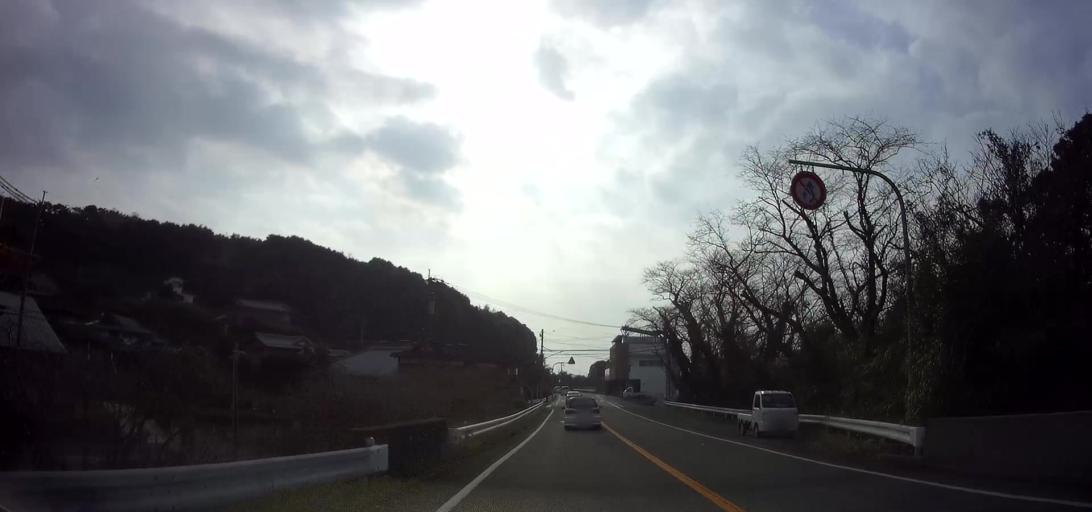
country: JP
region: Nagasaki
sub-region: Isahaya-shi
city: Isahaya
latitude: 32.7987
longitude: 130.1331
